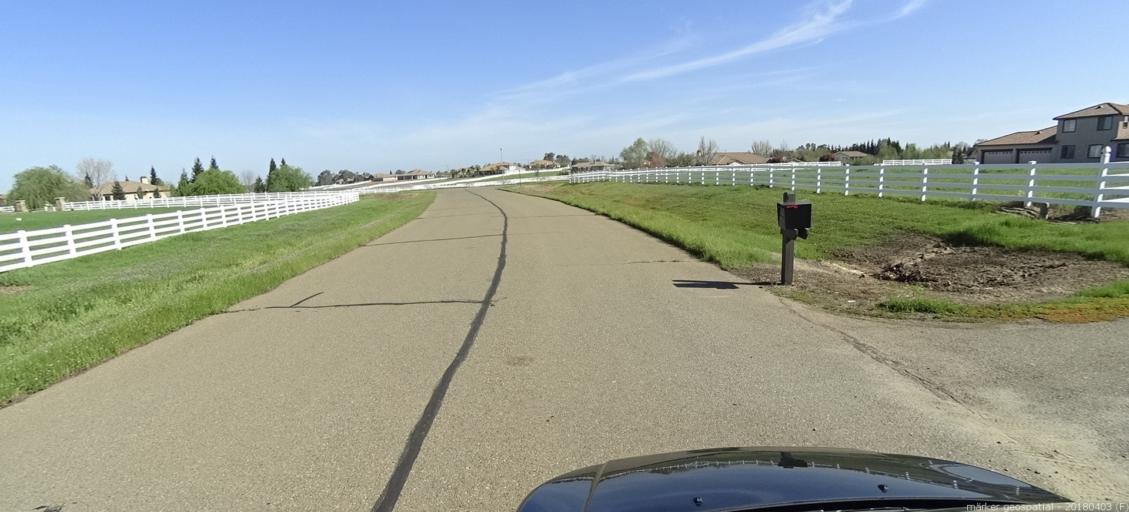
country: US
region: California
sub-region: Sacramento County
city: Wilton
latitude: 38.4177
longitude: -121.1936
